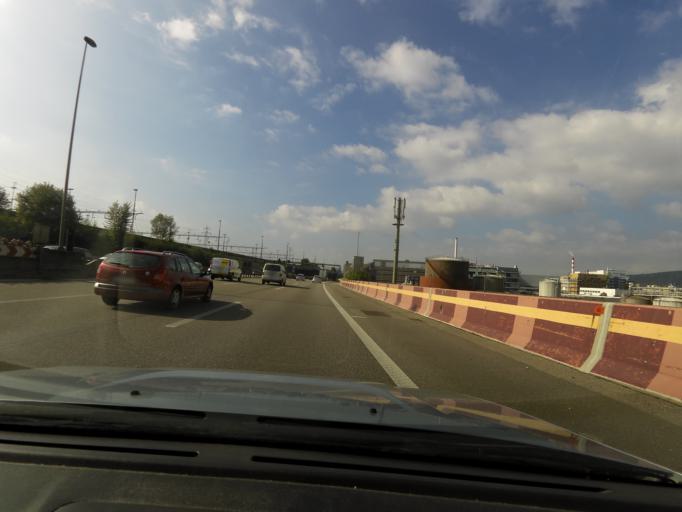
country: CH
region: Basel-Landschaft
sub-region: Bezirk Liestal
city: Pratteln
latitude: 47.5278
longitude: 7.6721
